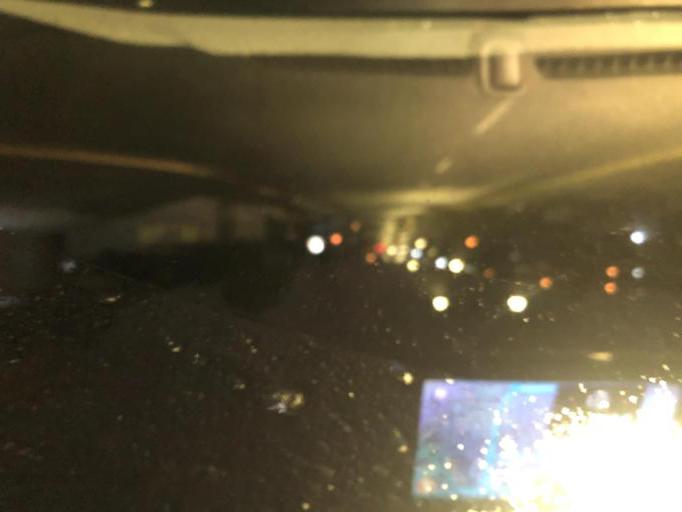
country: BR
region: Santa Catarina
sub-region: Joinville
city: Joinville
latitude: -26.3650
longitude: -48.8322
